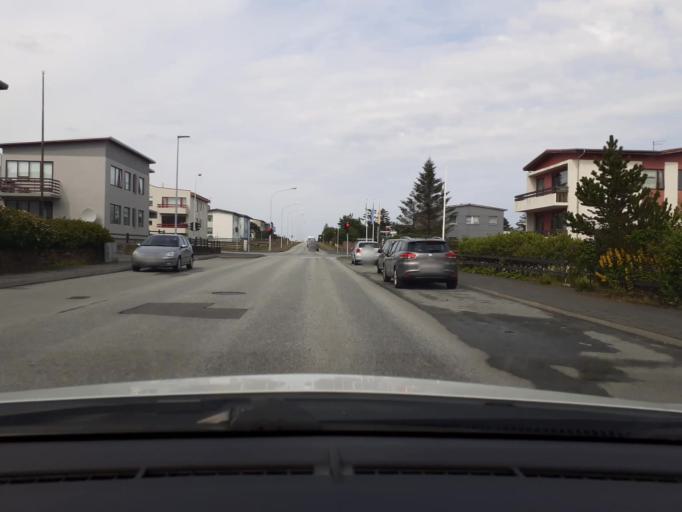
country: IS
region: Southern Peninsula
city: Reykjanesbaer
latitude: 64.0054
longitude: -22.5650
